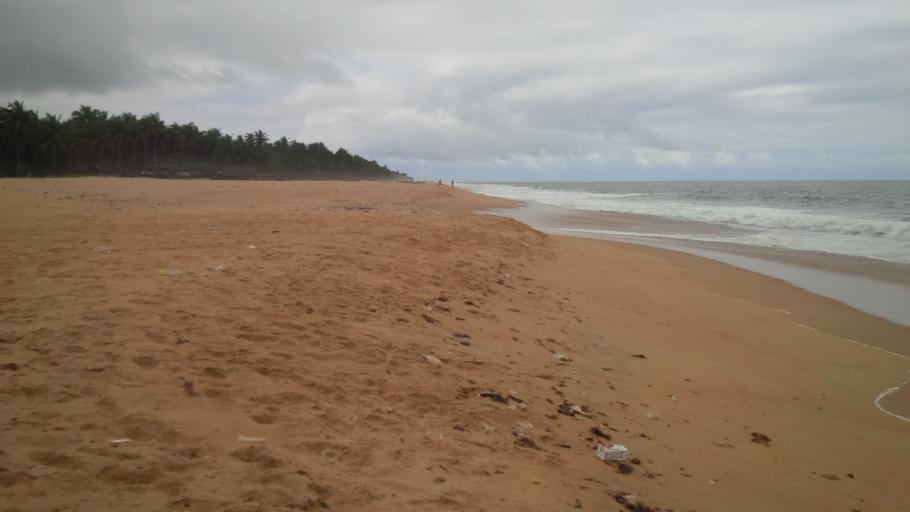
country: CI
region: Sud-Comoe
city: Grand-Bassam
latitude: 5.2212
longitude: -3.8405
